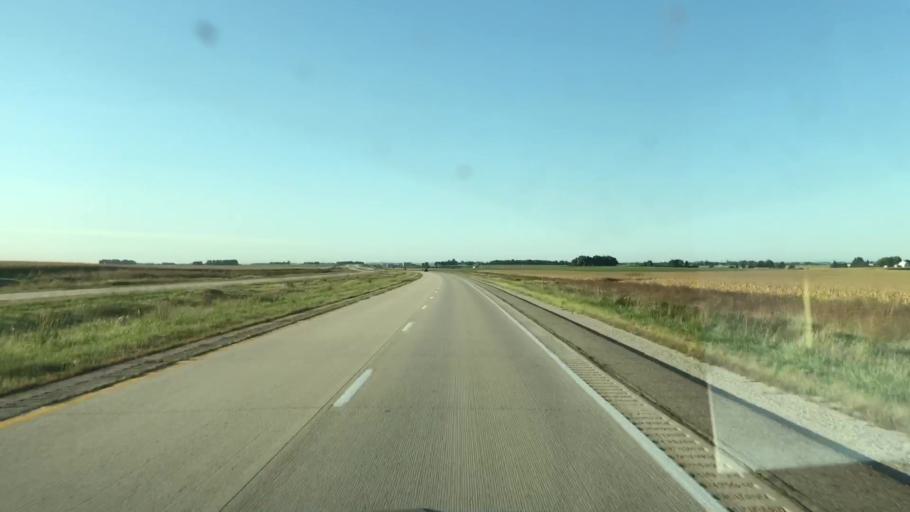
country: US
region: Iowa
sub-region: Osceola County
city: Sibley
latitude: 43.4590
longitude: -95.7131
